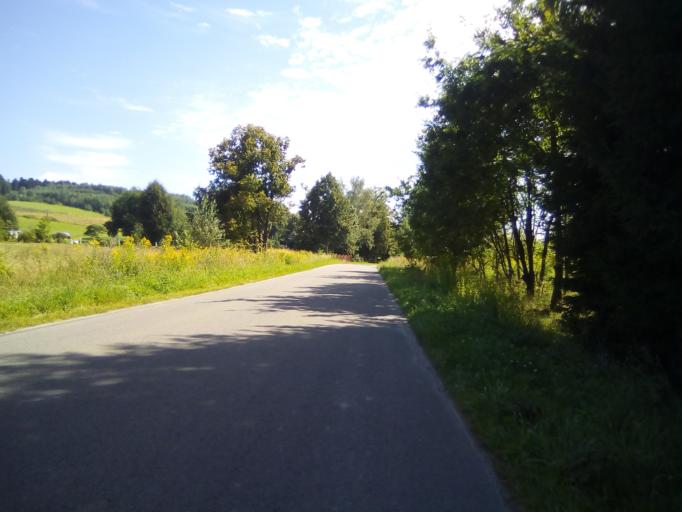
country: PL
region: Subcarpathian Voivodeship
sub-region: Powiat strzyzowski
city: Konieczkowa
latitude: 49.8236
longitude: 21.9262
